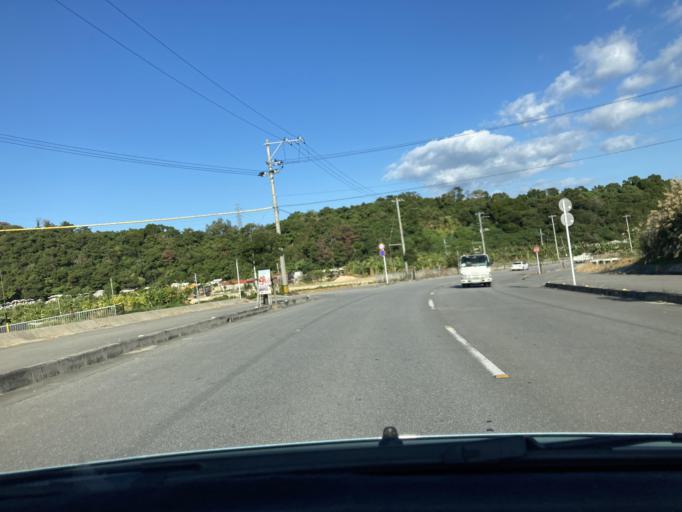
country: JP
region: Okinawa
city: Gushikawa
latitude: 26.3865
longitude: 127.8403
